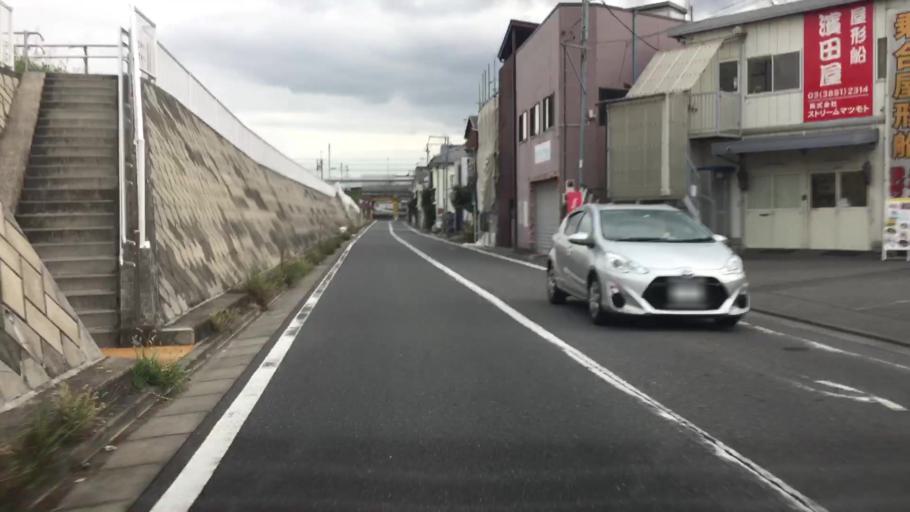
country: JP
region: Saitama
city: Soka
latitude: 35.7468
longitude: 139.8155
